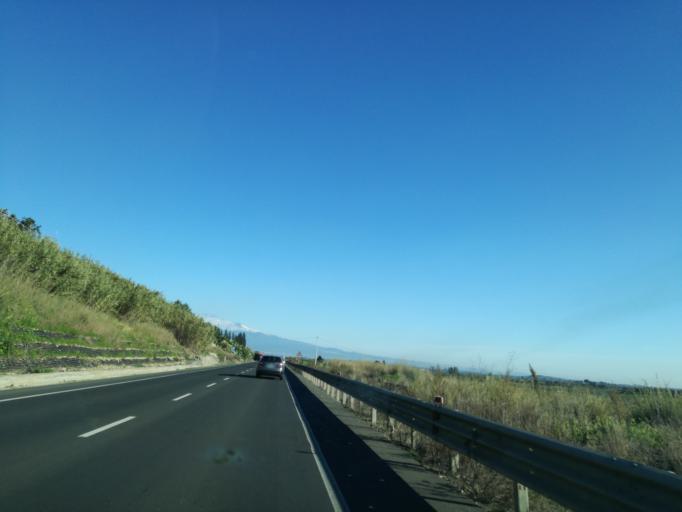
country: IT
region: Sicily
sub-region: Catania
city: Ramacca
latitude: 37.3706
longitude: 14.7241
